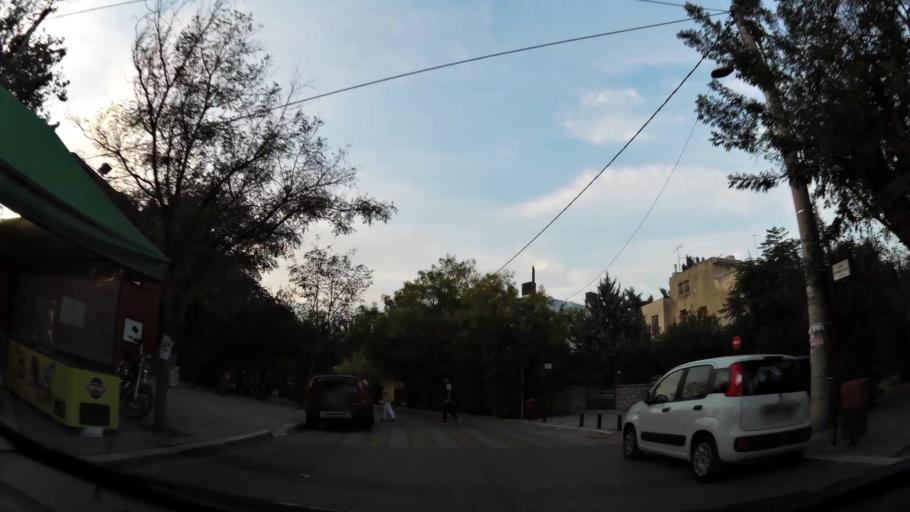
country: GR
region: Attica
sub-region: Nomarchia Athinas
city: Filothei
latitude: 38.0223
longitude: 23.7856
